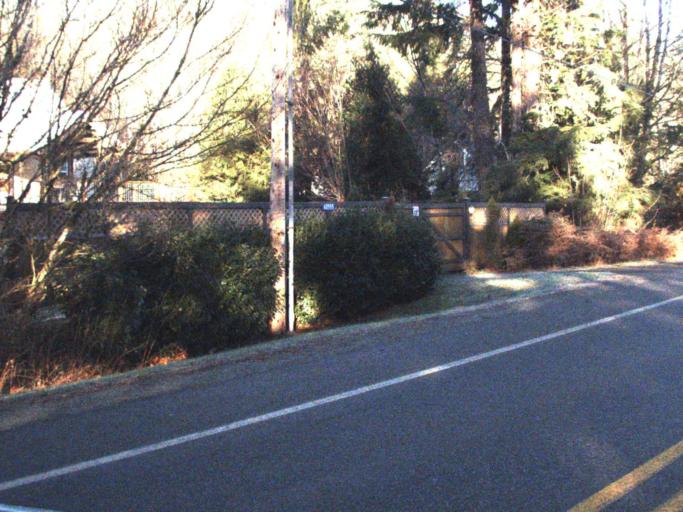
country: US
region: Washington
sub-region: Snohomish County
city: Darrington
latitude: 48.5431
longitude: -121.4252
